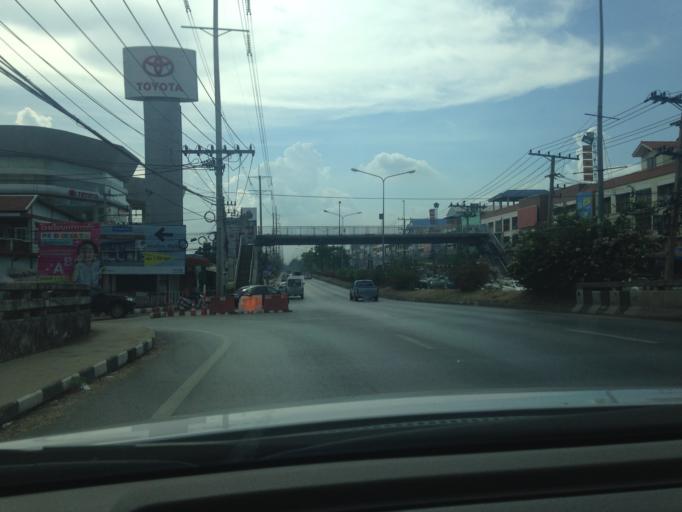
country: TH
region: Pathum Thani
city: Khlong Luang
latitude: 14.0659
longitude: 100.6637
